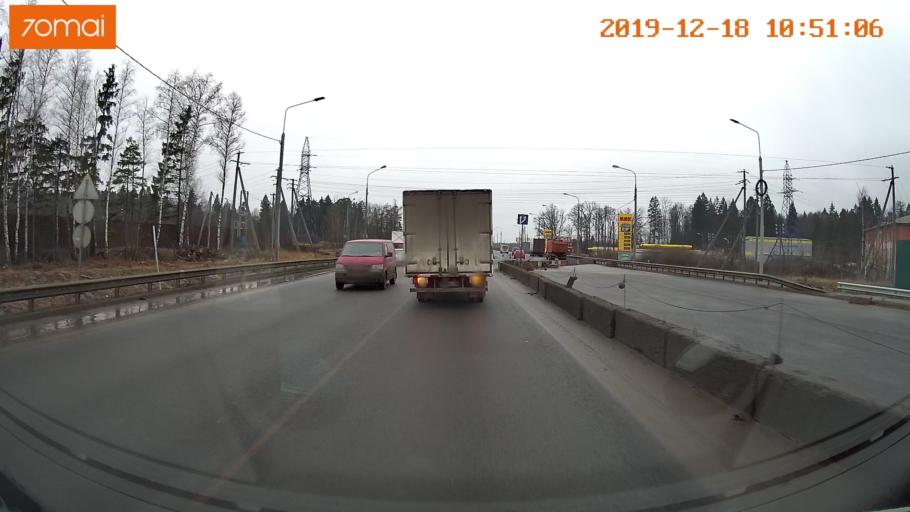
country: RU
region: Moskovskaya
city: Selyatino
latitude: 55.5128
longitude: 37.0006
